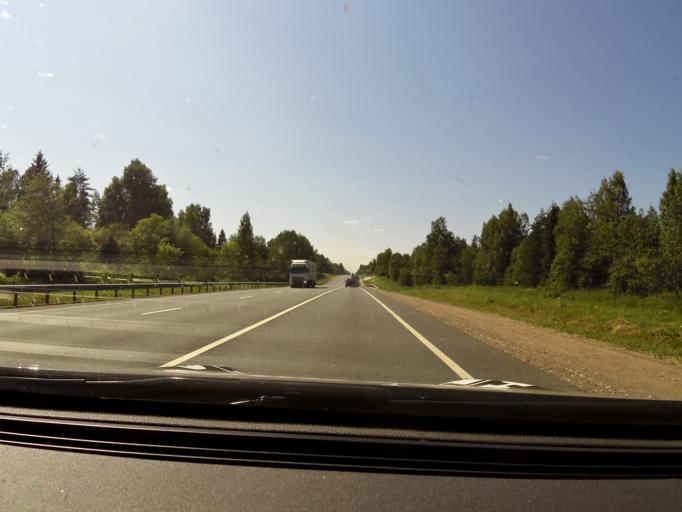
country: RU
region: Novgorod
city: Kresttsy
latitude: 58.3672
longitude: 32.1825
